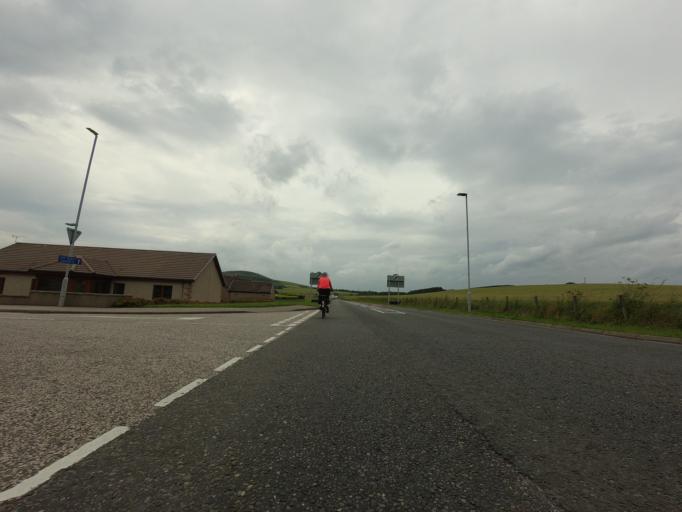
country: GB
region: Scotland
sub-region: Aberdeenshire
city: Portsoy
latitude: 57.6786
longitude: -2.6993
